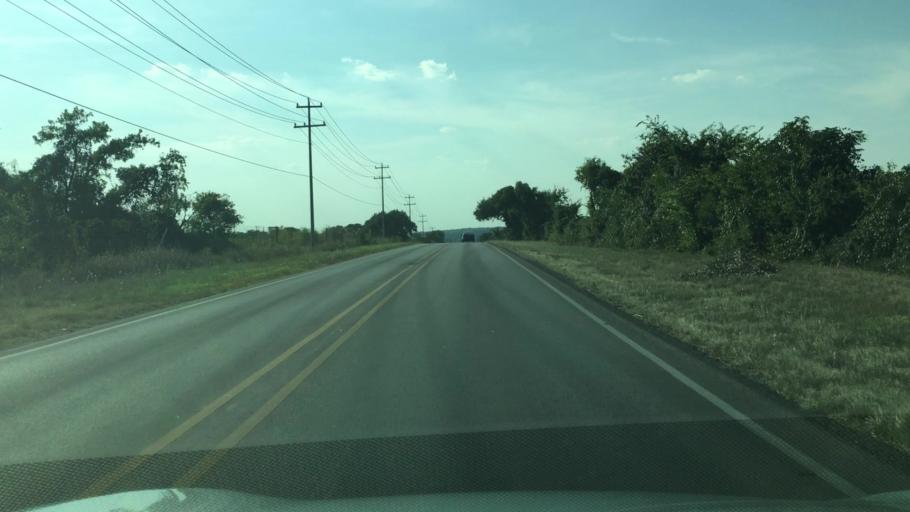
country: US
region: Texas
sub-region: Travis County
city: Shady Hollow
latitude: 30.1018
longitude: -97.9382
